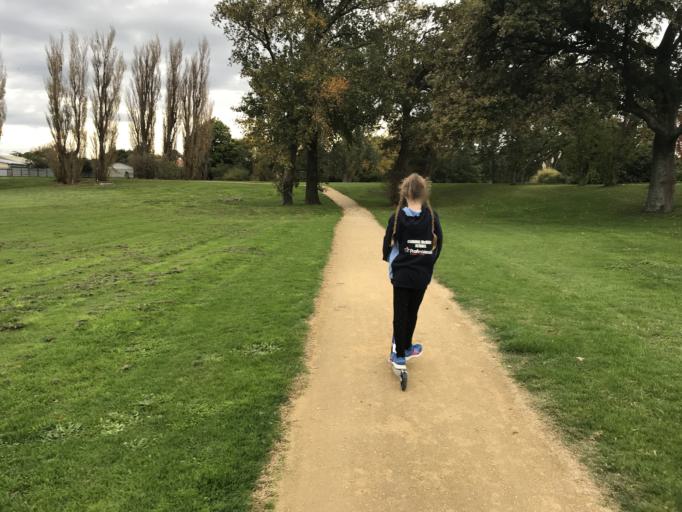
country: NZ
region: Manawatu-Wanganui
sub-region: Palmerston North City
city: Palmerston North
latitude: -40.3751
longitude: 175.5750
